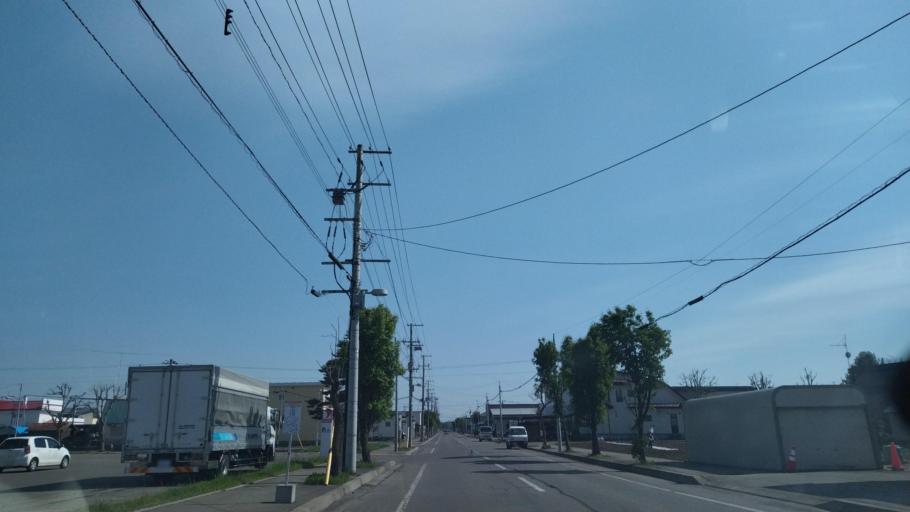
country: JP
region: Hokkaido
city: Obihiro
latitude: 42.9207
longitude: 143.0553
